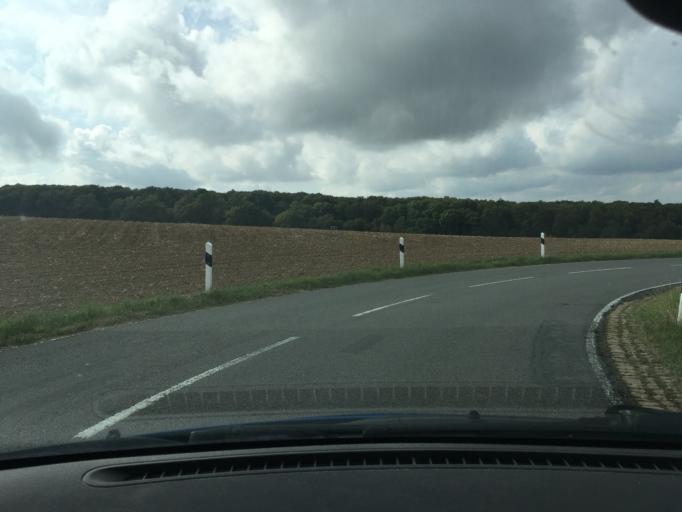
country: DE
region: Lower Saxony
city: Barsinghausen
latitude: 52.2509
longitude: 9.4437
